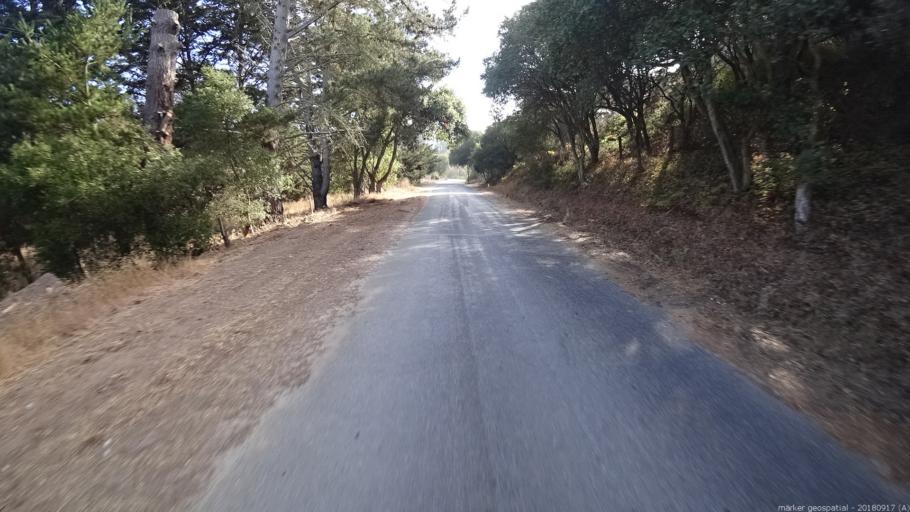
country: US
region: California
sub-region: Monterey County
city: Prunedale
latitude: 36.8038
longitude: -121.6975
